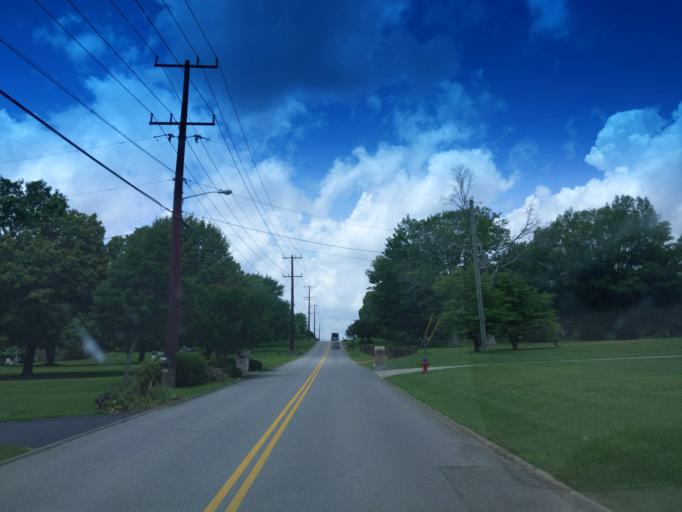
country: US
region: Tennessee
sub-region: Williamson County
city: Brentwood Estates
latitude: 36.0197
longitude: -86.7751
